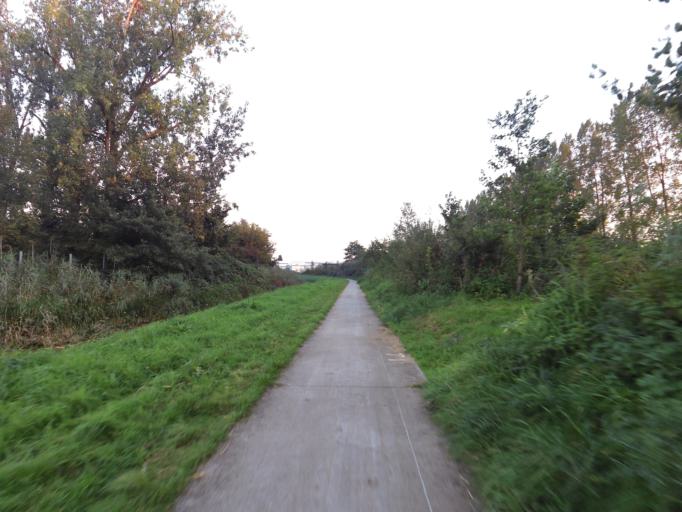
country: NL
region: Gelderland
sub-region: Gemeente Doetinchem
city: Doetinchem
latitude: 51.9262
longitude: 6.3321
